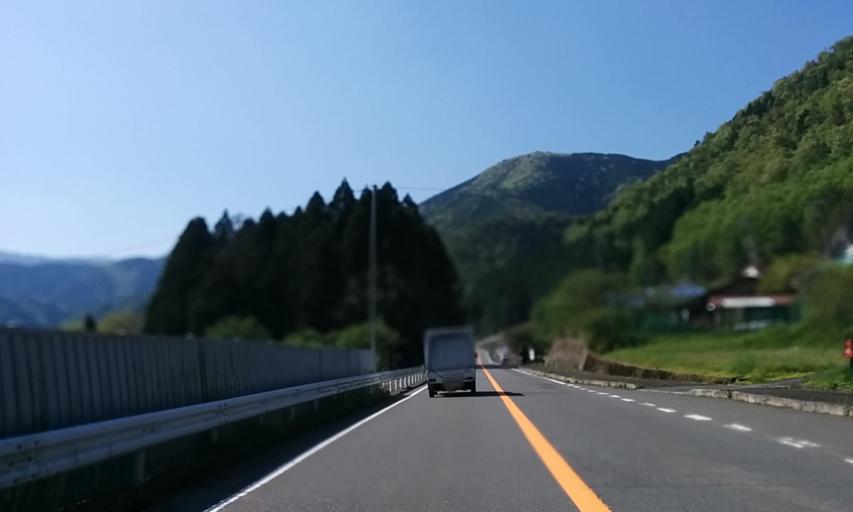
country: JP
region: Kyoto
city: Maizuru
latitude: 35.2770
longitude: 135.5432
